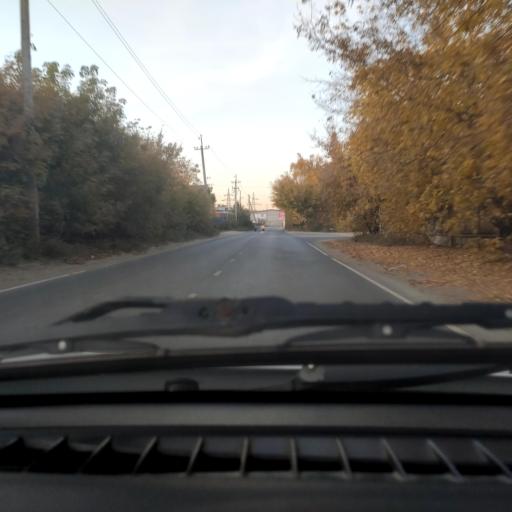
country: RU
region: Samara
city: Zhigulevsk
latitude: 53.5231
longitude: 49.4872
